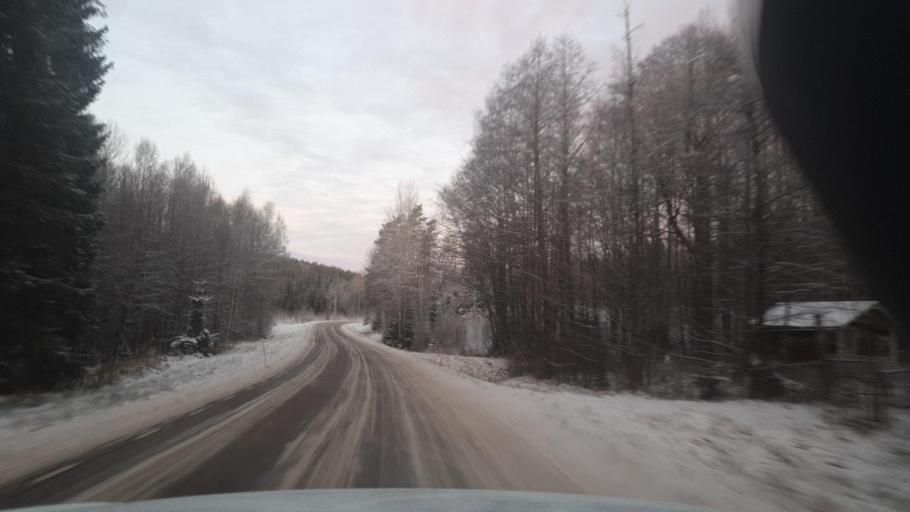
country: SE
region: Vaermland
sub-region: Grums Kommun
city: Slottsbron
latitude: 59.4495
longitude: 12.8506
